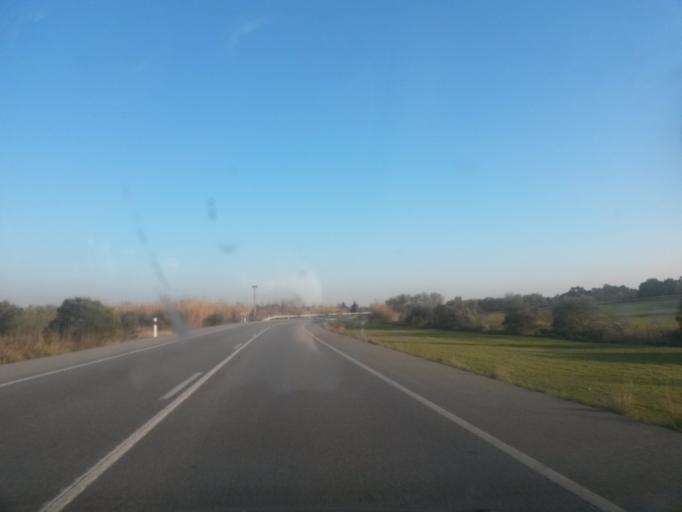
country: ES
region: Catalonia
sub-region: Provincia de Girona
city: Pont de Molins
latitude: 42.3279
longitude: 2.9319
